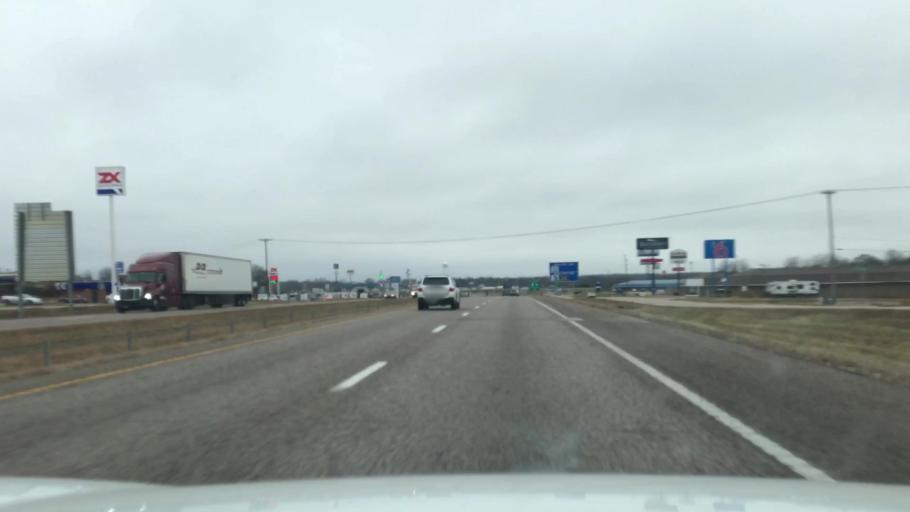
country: US
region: Missouri
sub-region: Franklin County
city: Sullivan
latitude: 38.2173
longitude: -91.1655
